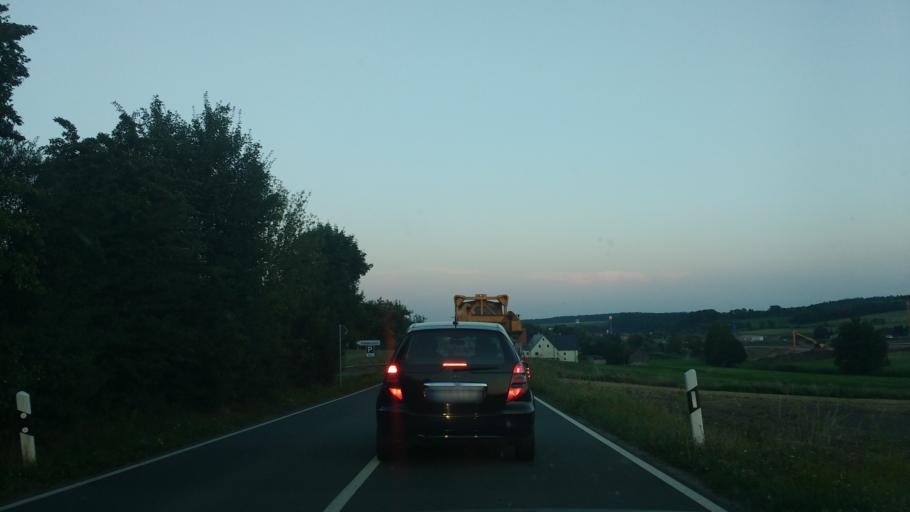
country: DE
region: Bavaria
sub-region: Regierungsbezirk Unterfranken
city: Geiselwind
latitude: 49.7782
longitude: 10.4569
